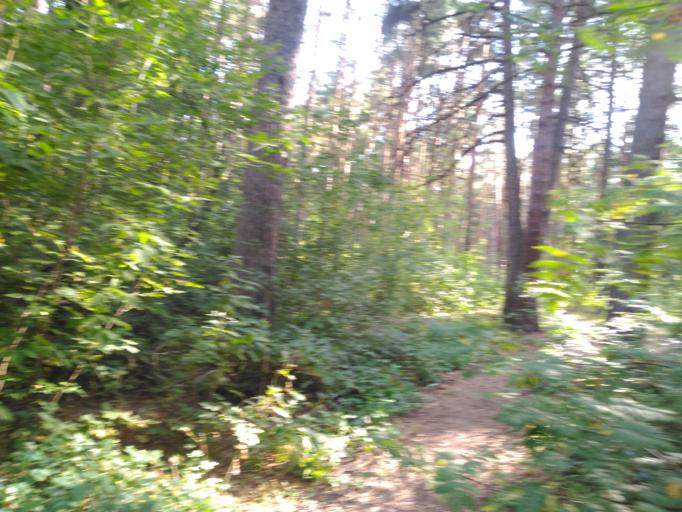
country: RU
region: Ulyanovsk
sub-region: Ulyanovskiy Rayon
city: Ulyanovsk
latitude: 54.3539
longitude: 48.5216
